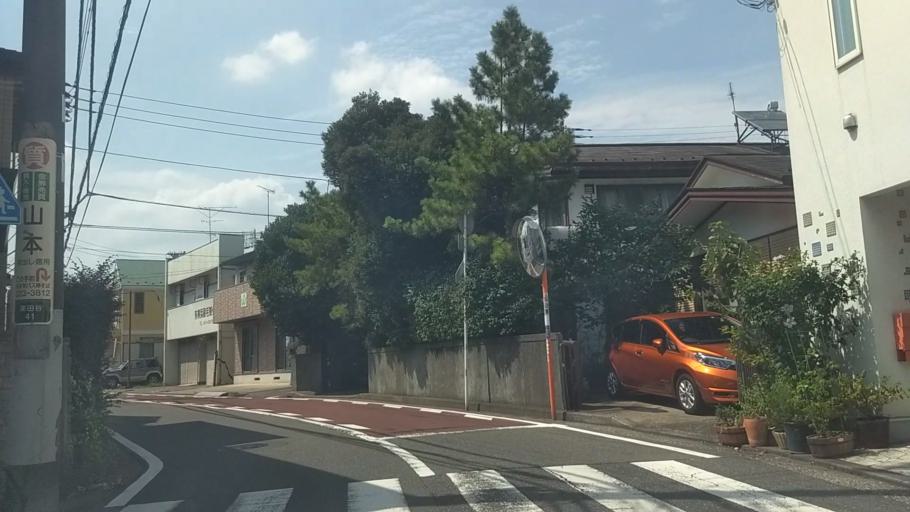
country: JP
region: Kanagawa
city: Yokohama
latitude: 35.4819
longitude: 139.6192
